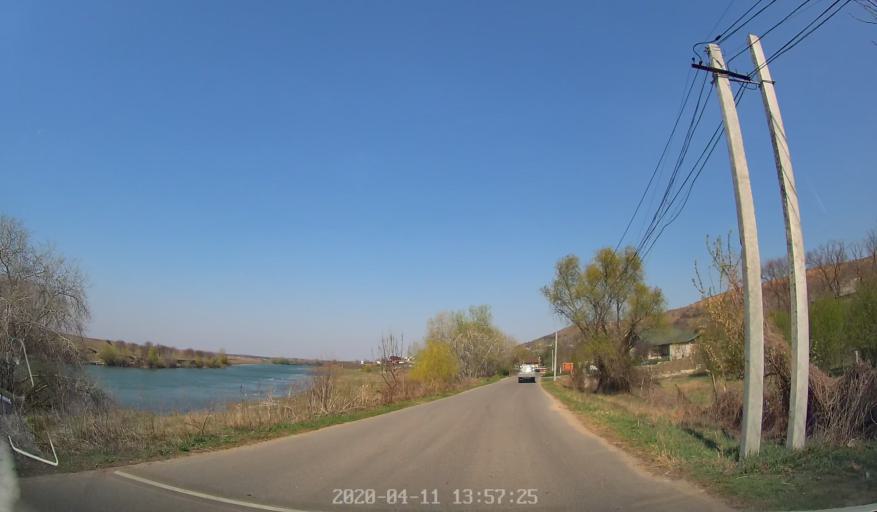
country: MD
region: Chisinau
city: Vadul lui Voda
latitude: 47.0753
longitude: 29.1272
